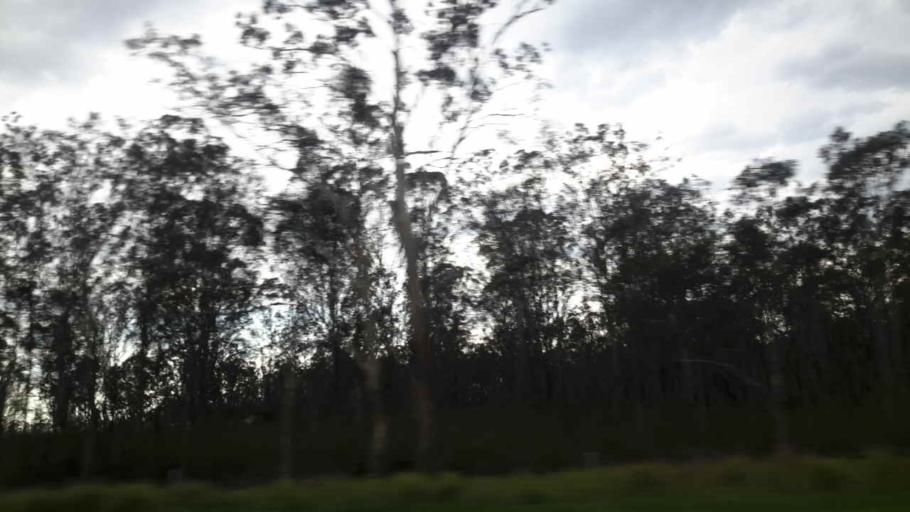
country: AU
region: New South Wales
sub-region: Camden
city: Narellan
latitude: -34.0155
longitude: 150.7243
